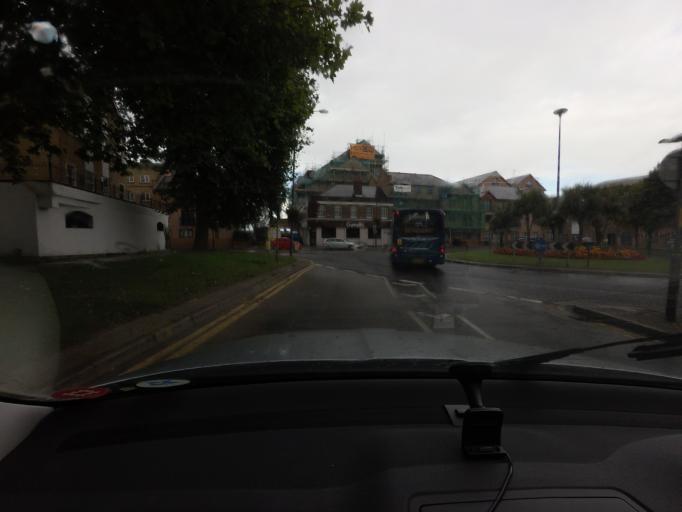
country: GB
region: England
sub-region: Kent
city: Gravesend
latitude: 51.4447
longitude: 0.3664
